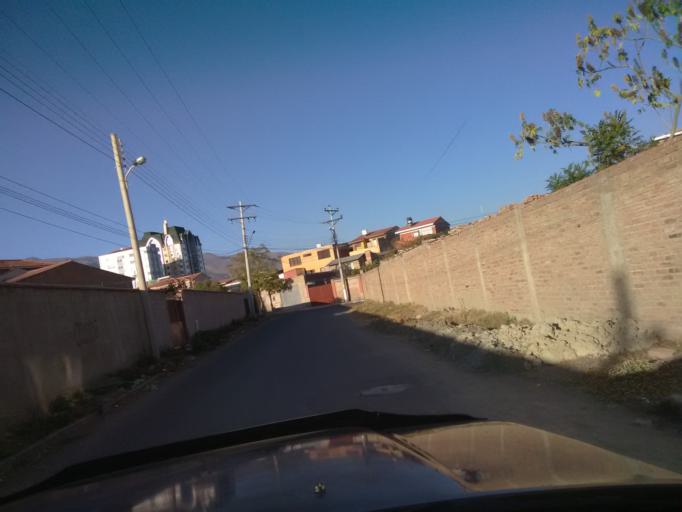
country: BO
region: Cochabamba
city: Cochabamba
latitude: -17.3717
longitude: -66.1908
